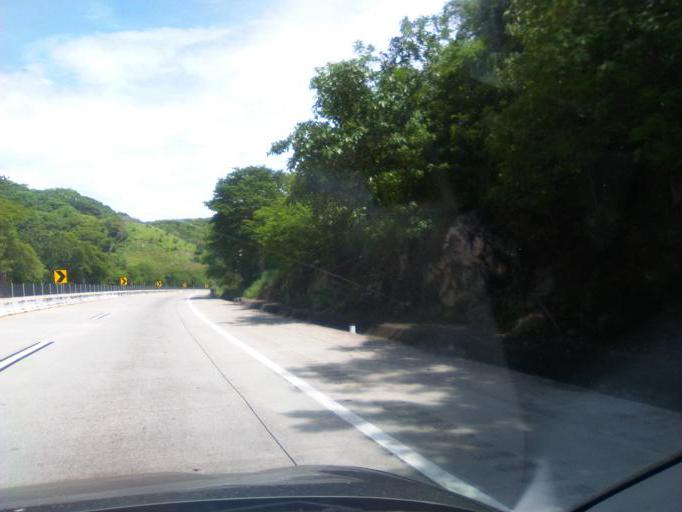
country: MX
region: Guerrero
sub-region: Acapulco de Juarez
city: Pueblo Madero (El Playon)
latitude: 17.0739
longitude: -99.6194
